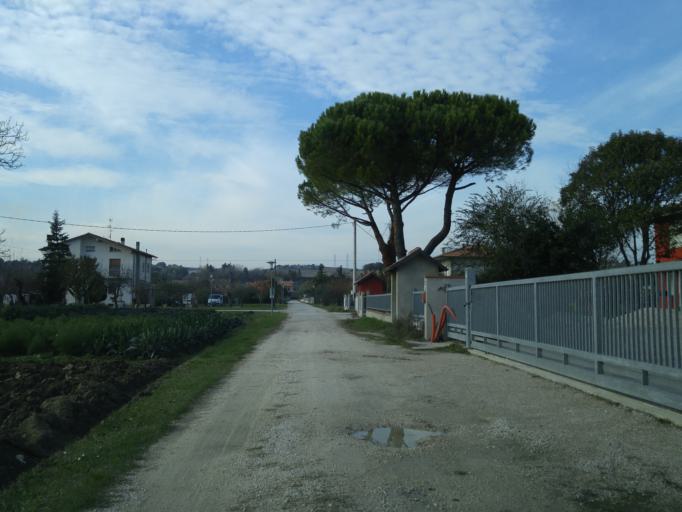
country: IT
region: The Marches
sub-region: Provincia di Pesaro e Urbino
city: Lucrezia
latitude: 43.7804
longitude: 12.9466
